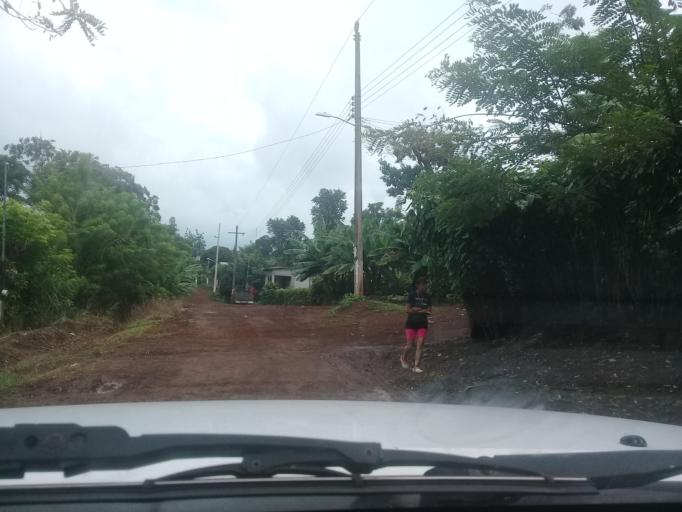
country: MX
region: Veracruz
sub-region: San Andres Tuxtla
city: Cerro las Iguanas
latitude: 18.4081
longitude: -95.2004
